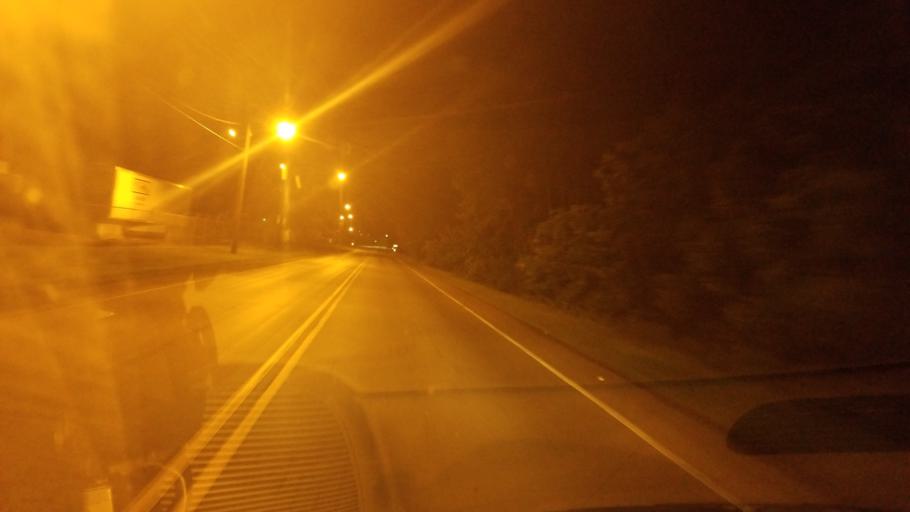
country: US
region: Ohio
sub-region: Trumbull County
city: Niles
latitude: 41.1676
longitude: -80.7662
